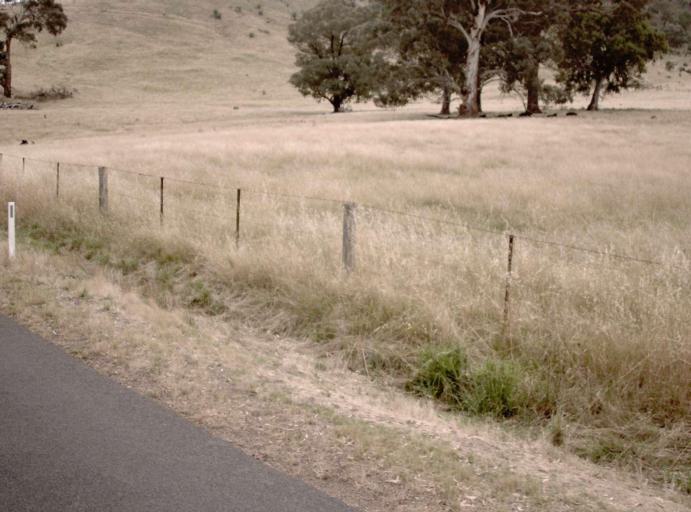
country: AU
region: Victoria
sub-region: Wellington
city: Heyfield
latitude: -37.6595
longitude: 146.6460
